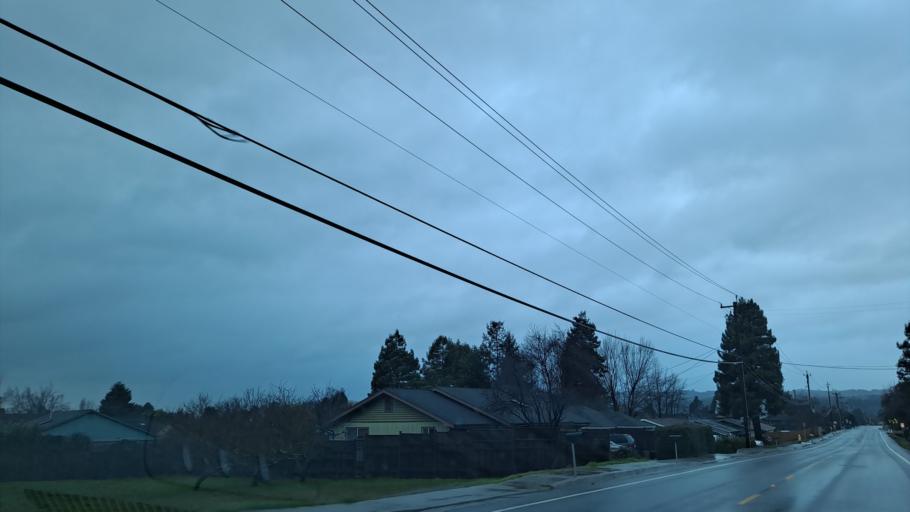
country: US
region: California
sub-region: Humboldt County
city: Fortuna
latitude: 40.5744
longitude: -124.1281
